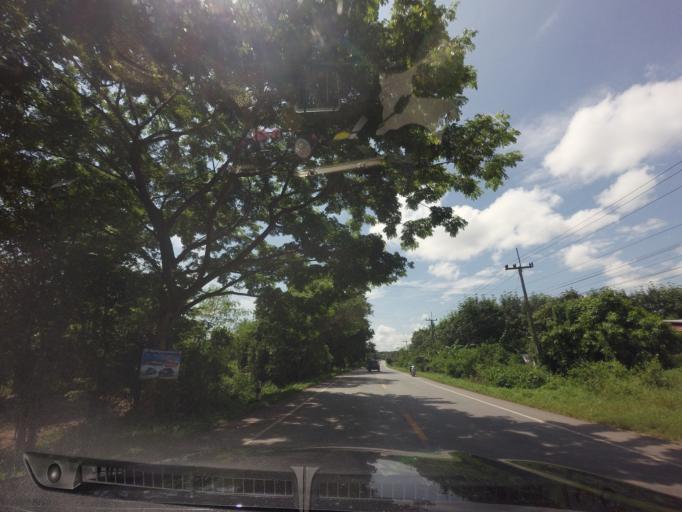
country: TH
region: Changwat Udon Thani
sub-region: Amphoe Ban Phue
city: Ban Phue
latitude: 17.7228
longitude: 102.3937
